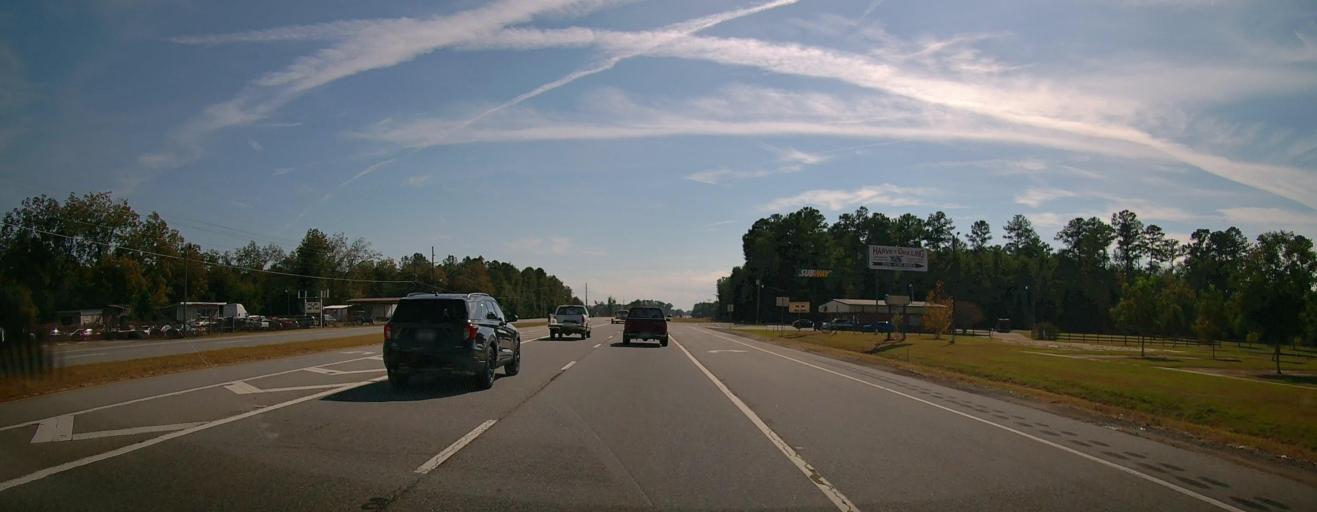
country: US
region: Georgia
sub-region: Dougherty County
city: Putney
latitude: 31.4998
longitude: -84.1156
